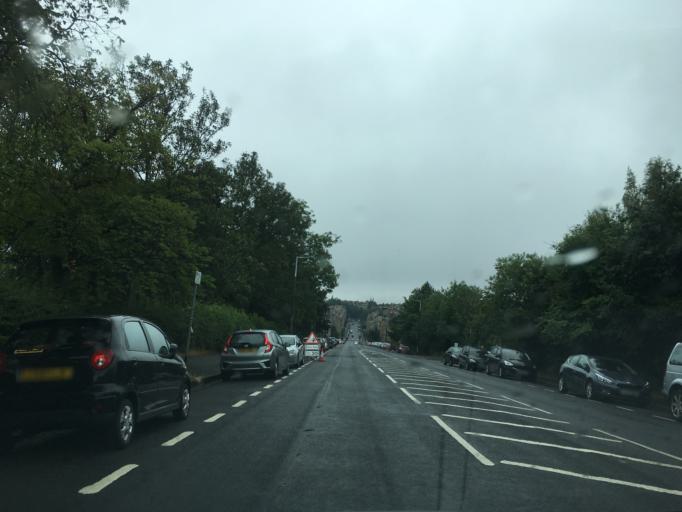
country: GB
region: Scotland
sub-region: Edinburgh
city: Edinburgh
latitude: 55.9619
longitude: -3.2203
